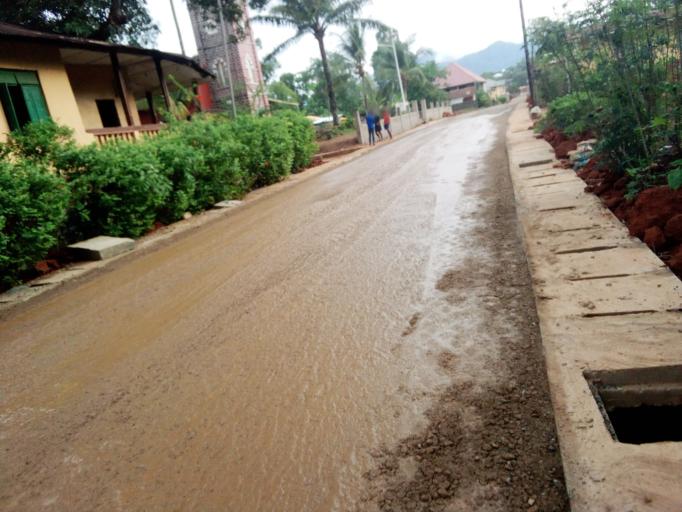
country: SL
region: Western Area
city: Waterloo
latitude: 8.3407
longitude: -13.0699
